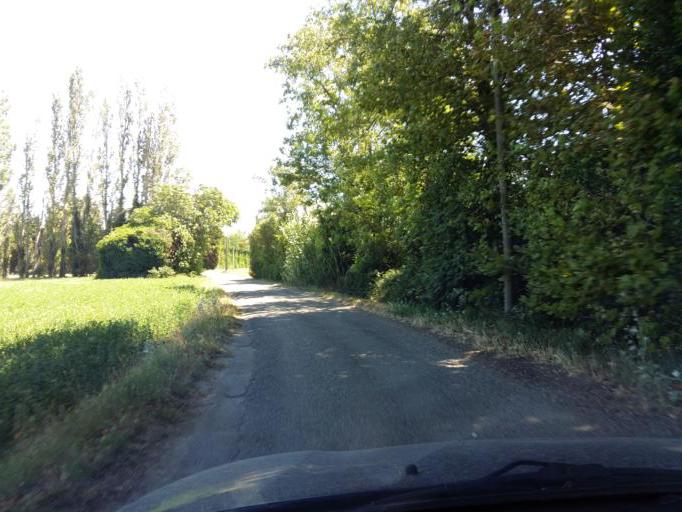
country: FR
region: Provence-Alpes-Cote d'Azur
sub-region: Departement du Vaucluse
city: Mornas
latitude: 44.1706
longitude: 4.7307
